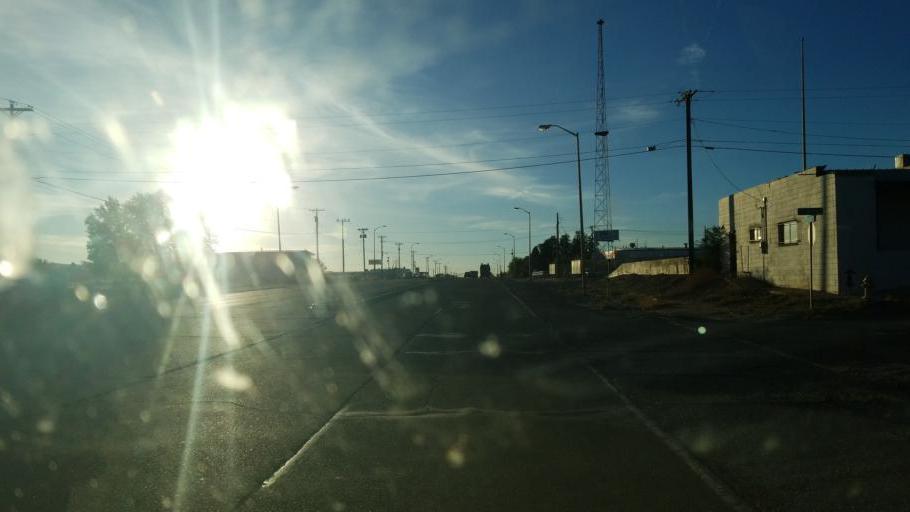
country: US
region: New Mexico
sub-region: San Juan County
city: Farmington
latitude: 36.7193
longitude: -108.1629
